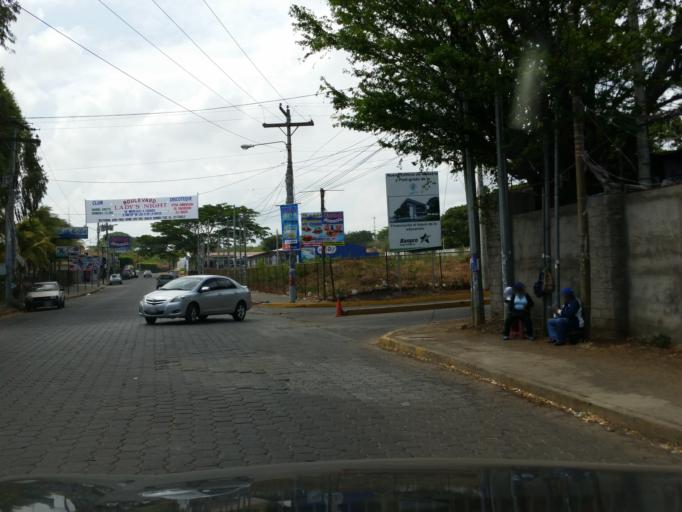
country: NI
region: Managua
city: Managua
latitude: 12.1118
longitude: -86.2564
